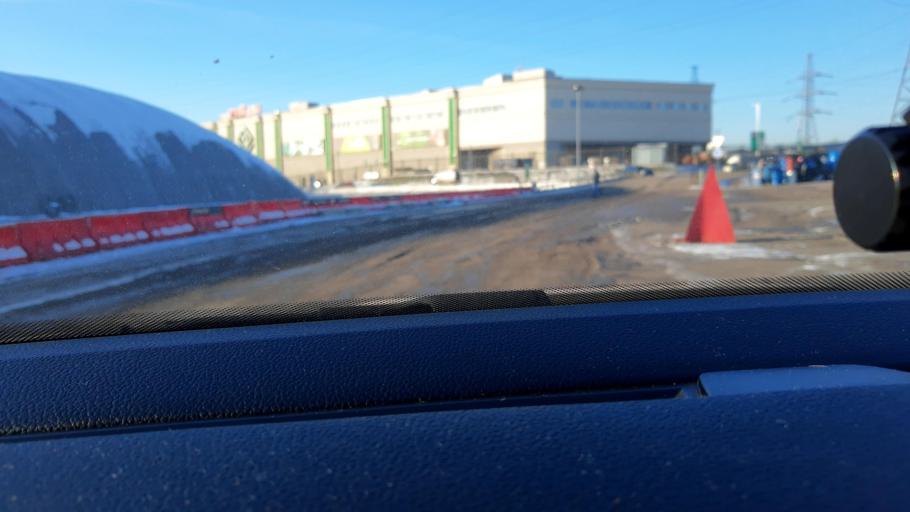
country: RU
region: Moscow
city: Vatutino
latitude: 55.8985
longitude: 37.6789
